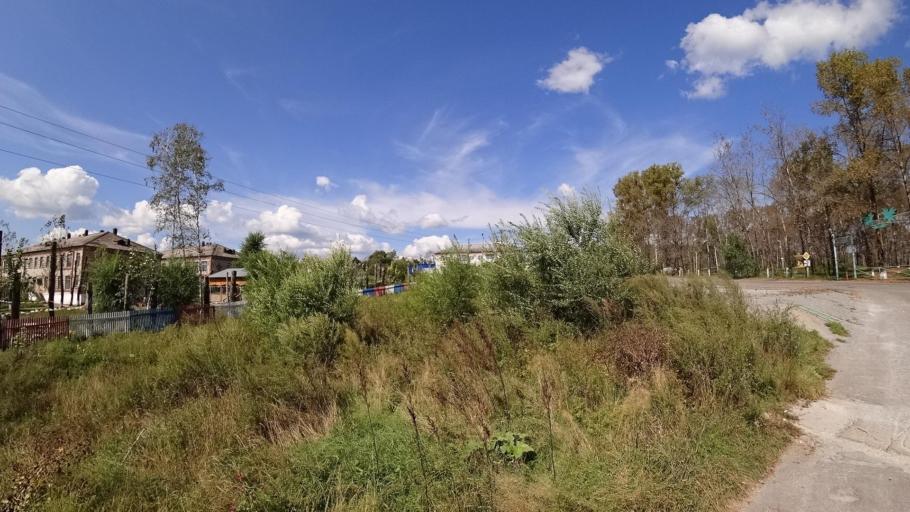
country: RU
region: Jewish Autonomous Oblast
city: Londoko
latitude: 49.0156
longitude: 131.8872
